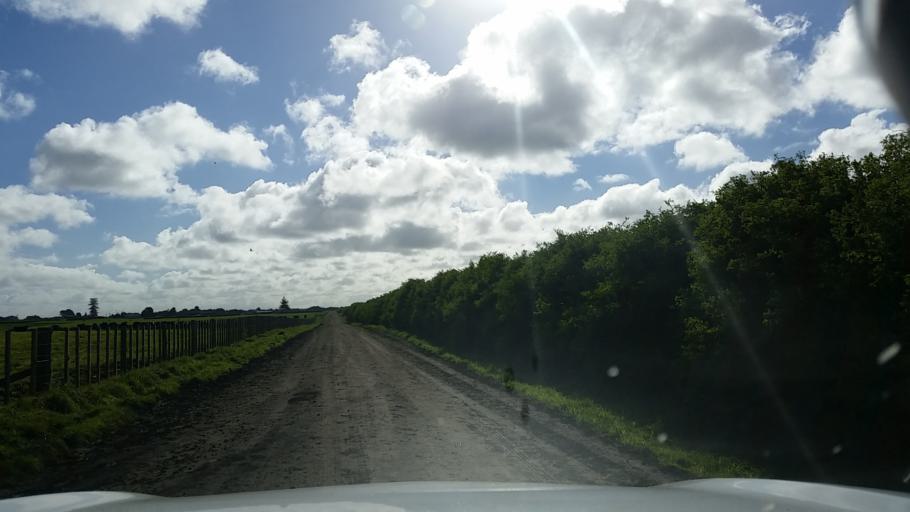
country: NZ
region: Taranaki
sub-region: South Taranaki District
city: Patea
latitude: -39.7553
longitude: 174.5228
